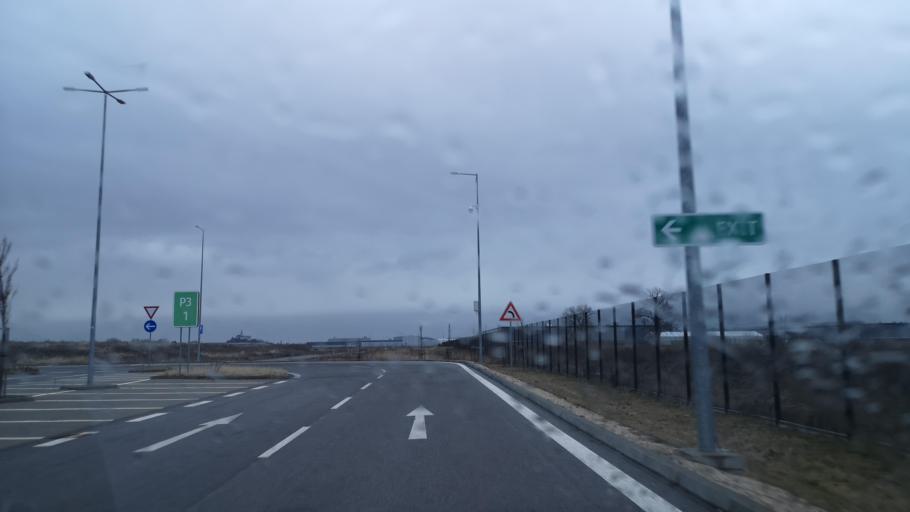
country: SK
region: Nitriansky
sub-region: Okres Nitra
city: Nitra
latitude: 48.3443
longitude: 18.0526
